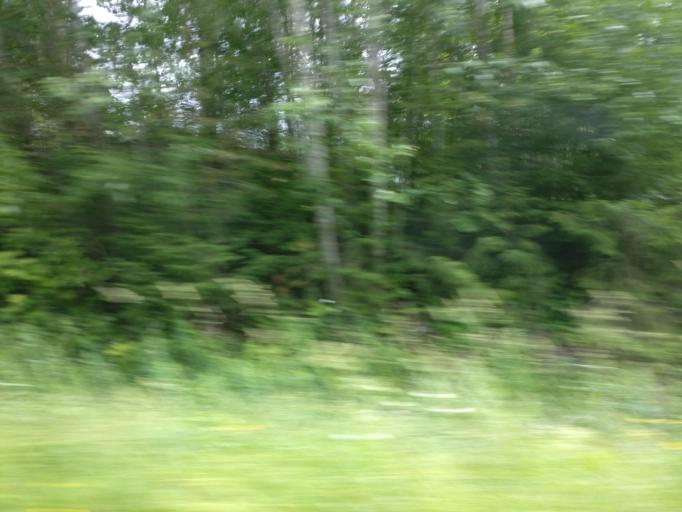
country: FI
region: Northern Savo
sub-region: Koillis-Savo
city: Juankoski
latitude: 62.9636
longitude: 28.2232
